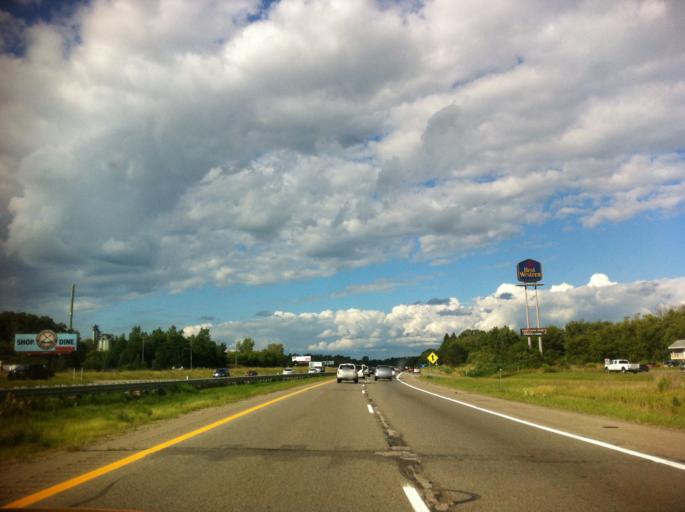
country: US
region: Michigan
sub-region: Livingston County
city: Whitmore Lake
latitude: 42.4301
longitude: -83.7659
